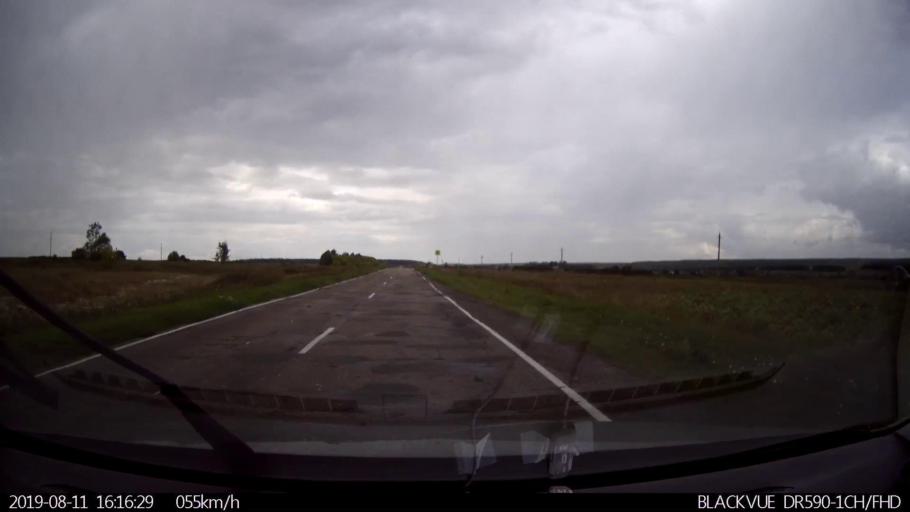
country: RU
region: Ulyanovsk
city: Mayna
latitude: 54.0415
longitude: 47.6211
